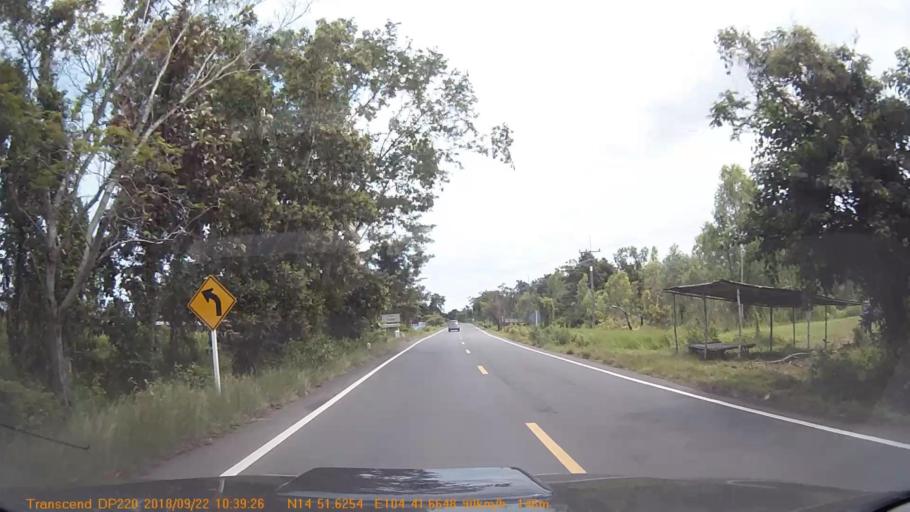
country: TH
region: Sisaket
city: Non Kho
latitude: 14.8605
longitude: 104.6945
